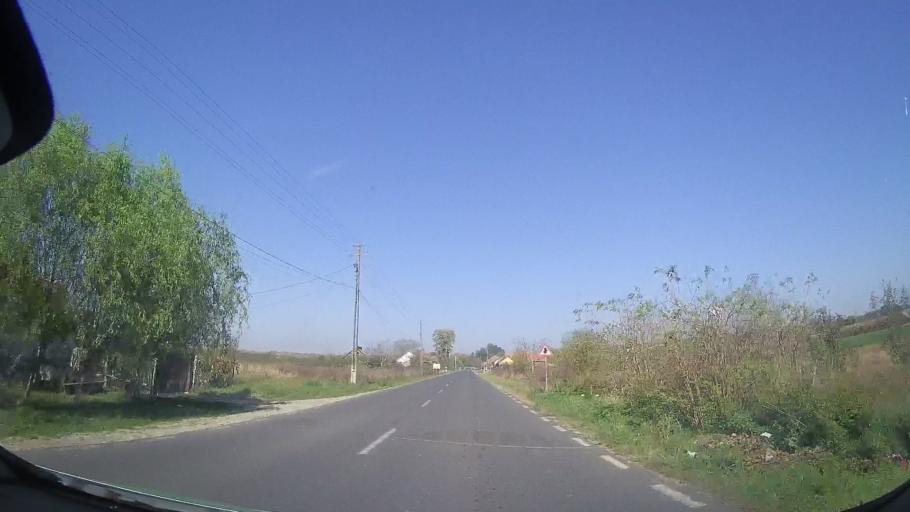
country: RO
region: Timis
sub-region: Comuna Balint
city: Balint
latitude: 45.8071
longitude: 21.8604
